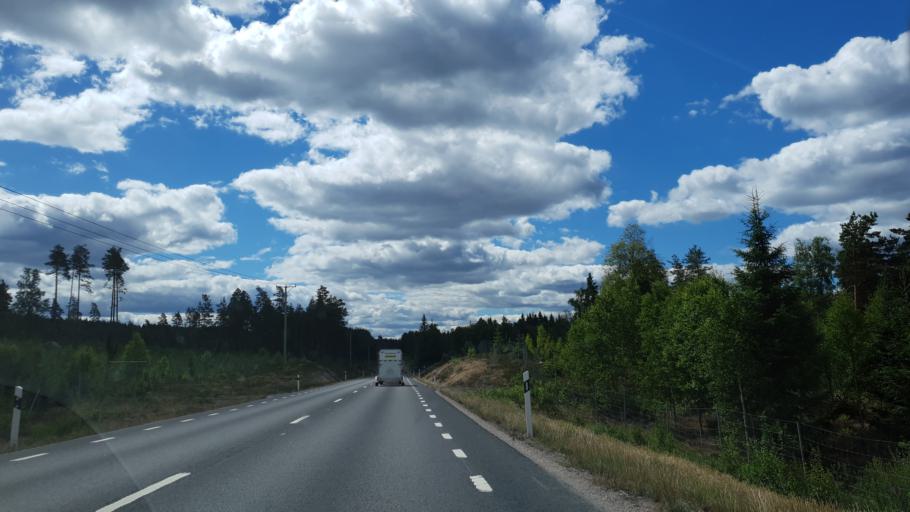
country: SE
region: Kronoberg
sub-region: Vaxjo Kommun
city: Braas
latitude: 57.1894
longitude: 15.1564
